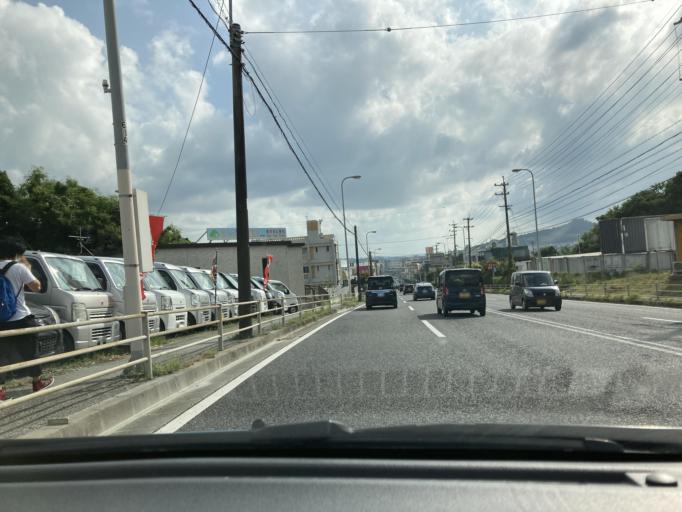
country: JP
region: Okinawa
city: Ginowan
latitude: 26.2314
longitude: 127.7690
